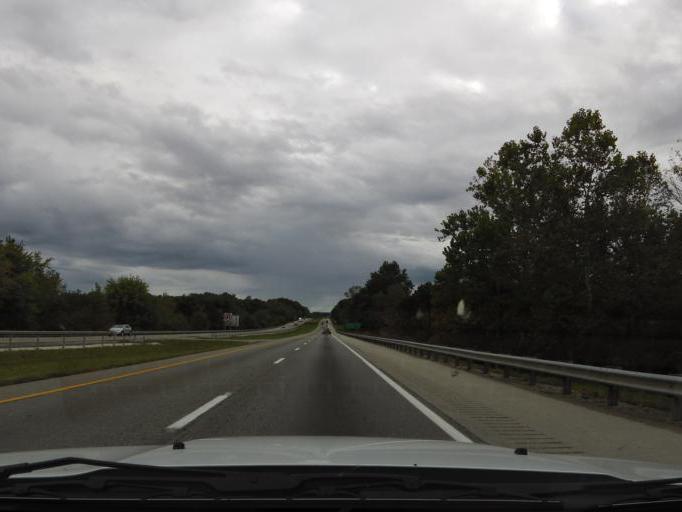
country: US
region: Kentucky
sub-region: Whitley County
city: Corbin
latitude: 36.9317
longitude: -84.1261
